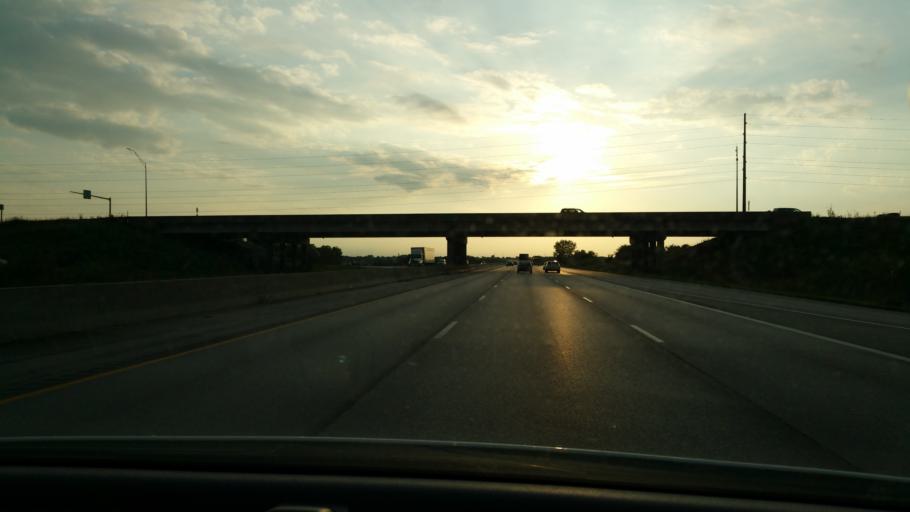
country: US
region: Iowa
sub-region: Polk County
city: Urbandale
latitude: 41.6523
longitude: -93.7350
